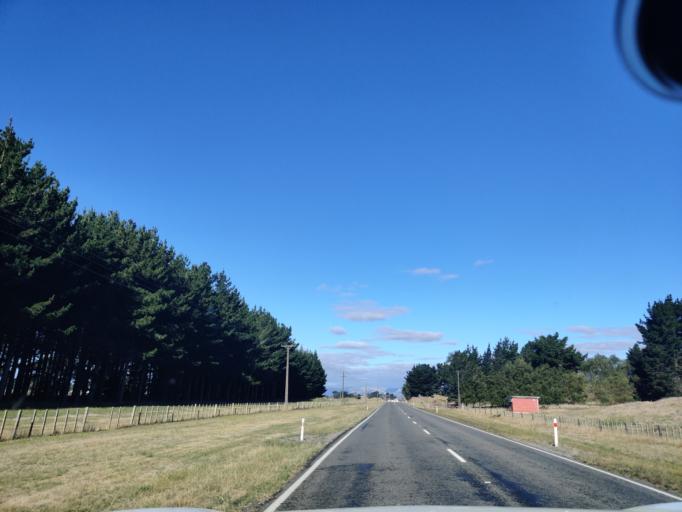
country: NZ
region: Manawatu-Wanganui
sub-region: Horowhenua District
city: Foxton
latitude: -40.4026
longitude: 175.3638
